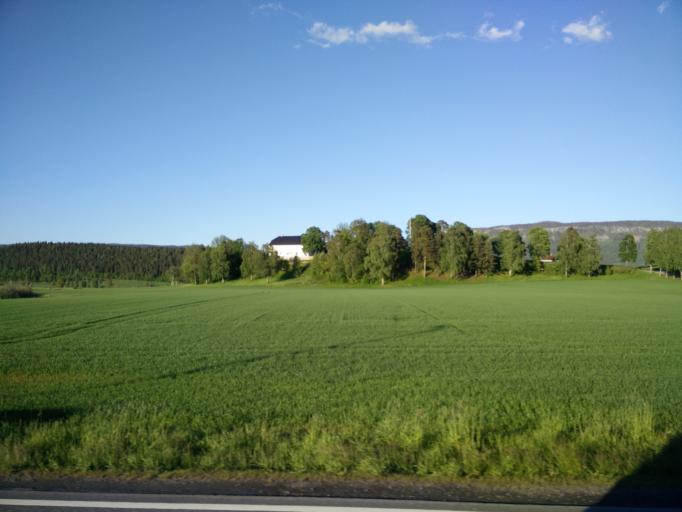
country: NO
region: Buskerud
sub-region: Hole
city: Vik
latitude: 60.1004
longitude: 10.2900
